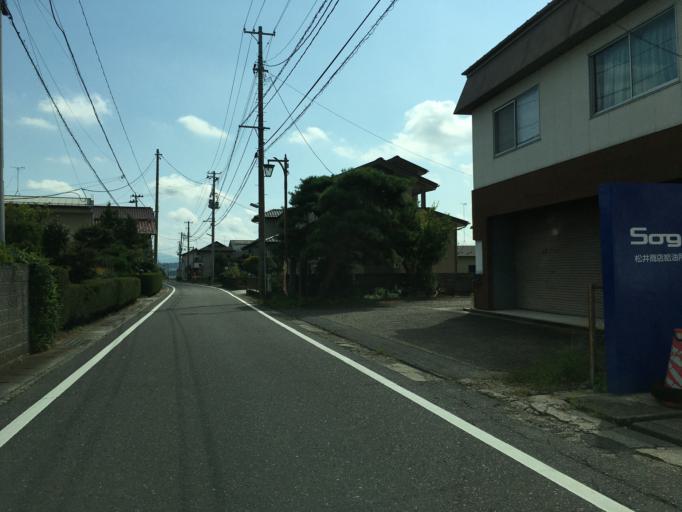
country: JP
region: Fukushima
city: Motomiya
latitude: 37.5291
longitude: 140.3693
